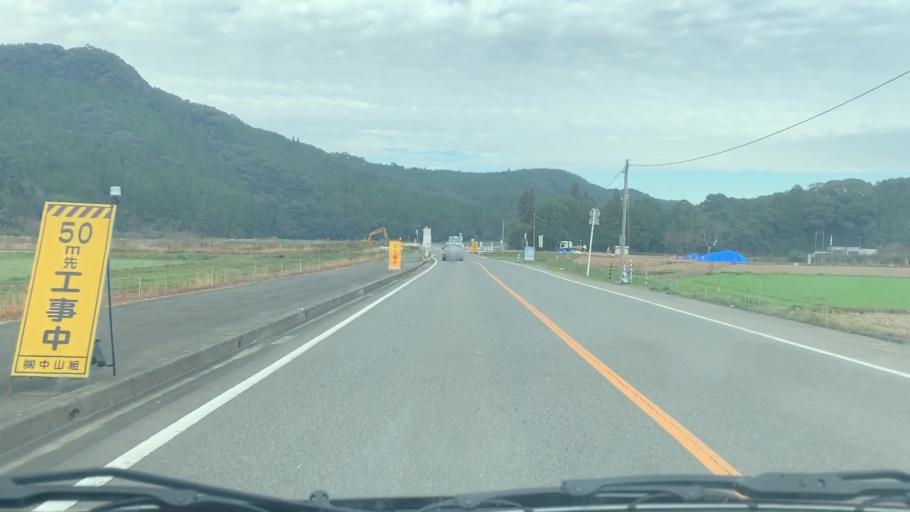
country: JP
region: Saga Prefecture
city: Takeocho-takeo
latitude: 33.2459
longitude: 129.9694
